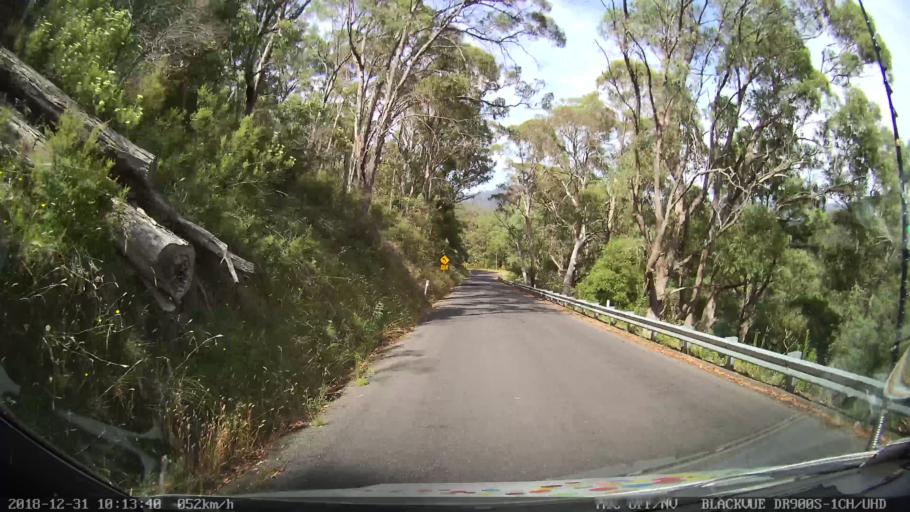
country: AU
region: New South Wales
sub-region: Snowy River
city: Jindabyne
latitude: -36.5387
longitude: 148.1532
